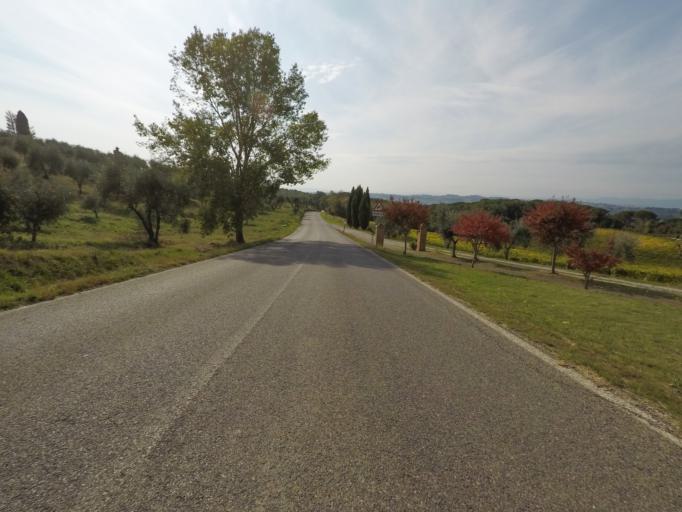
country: IT
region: Tuscany
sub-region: Provincia di Siena
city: Belverde
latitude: 43.3908
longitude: 11.3450
